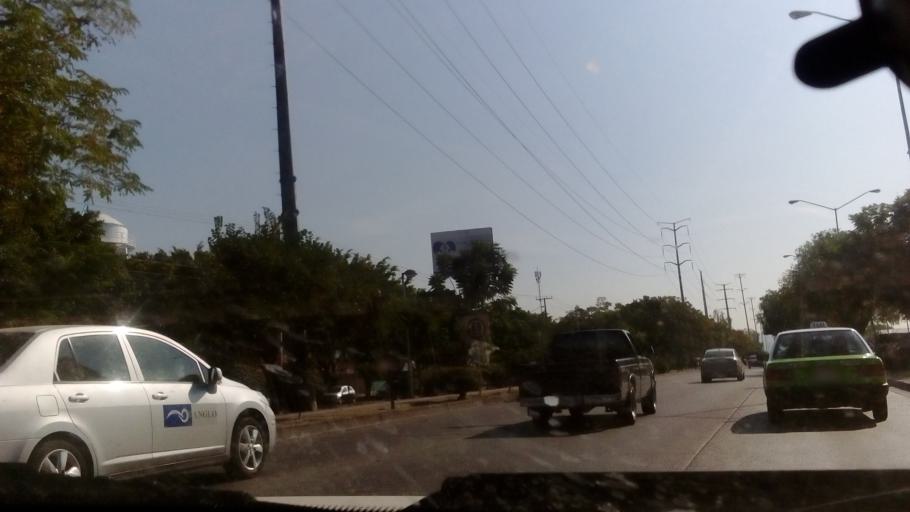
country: MX
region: Guanajuato
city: Leon
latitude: 21.1485
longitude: -101.6606
